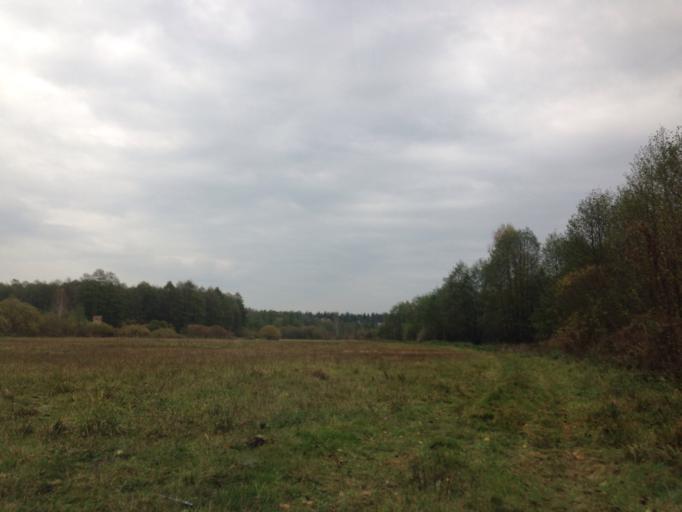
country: PL
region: Kujawsko-Pomorskie
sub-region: Powiat brodnicki
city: Brzozie
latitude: 53.2925
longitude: 19.5550
